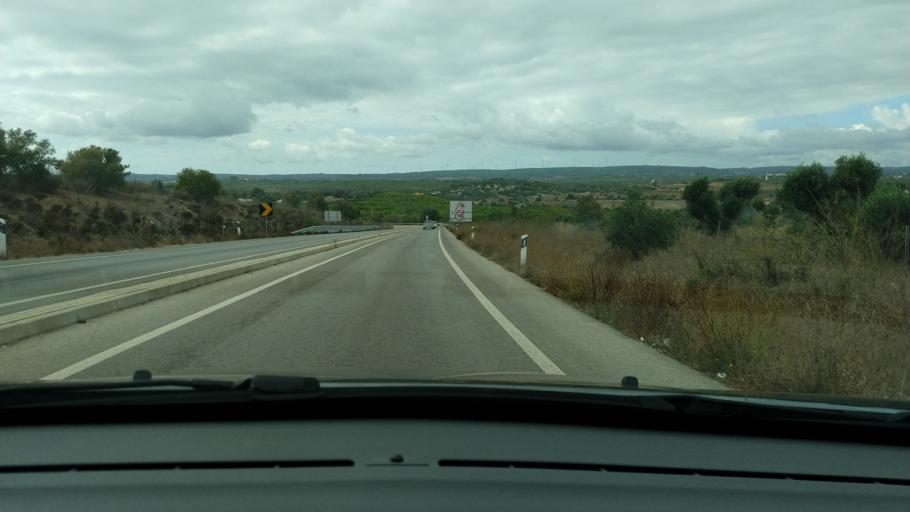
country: PT
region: Faro
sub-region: Lagos
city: Lagos
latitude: 37.0982
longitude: -8.7443
